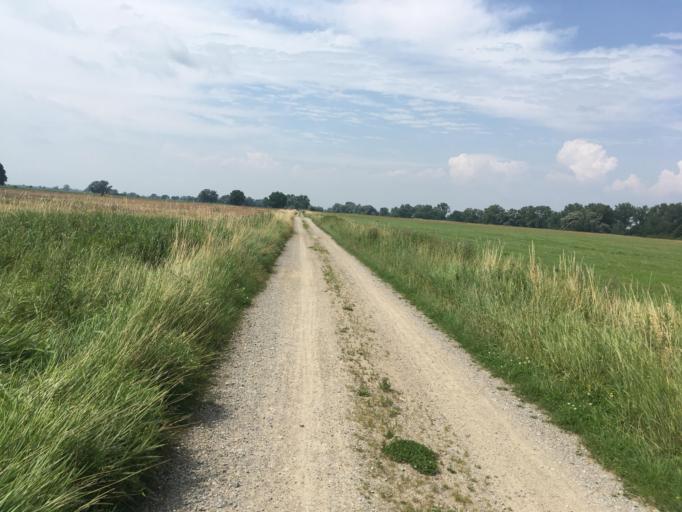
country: DE
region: Lower Saxony
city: Bleckede
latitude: 53.2804
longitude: 10.7936
